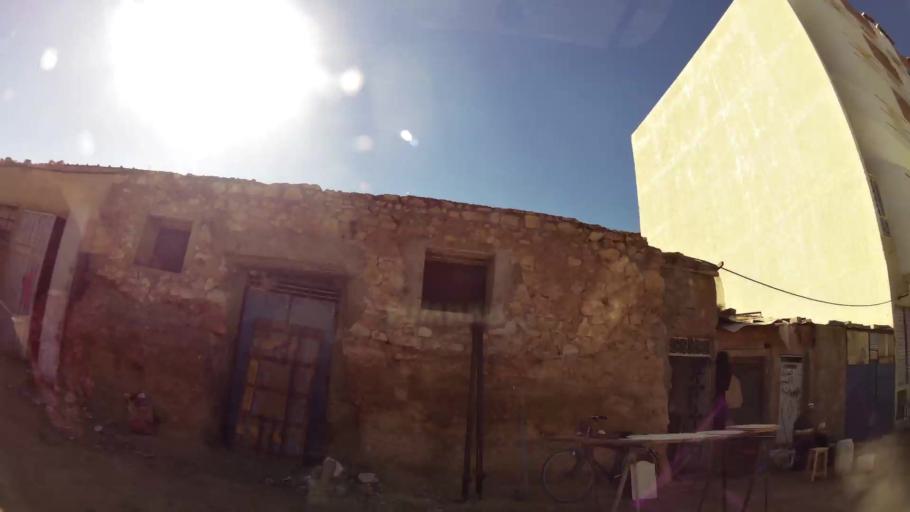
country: MA
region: Meknes-Tafilalet
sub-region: Meknes
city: Meknes
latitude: 33.8775
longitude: -5.5788
